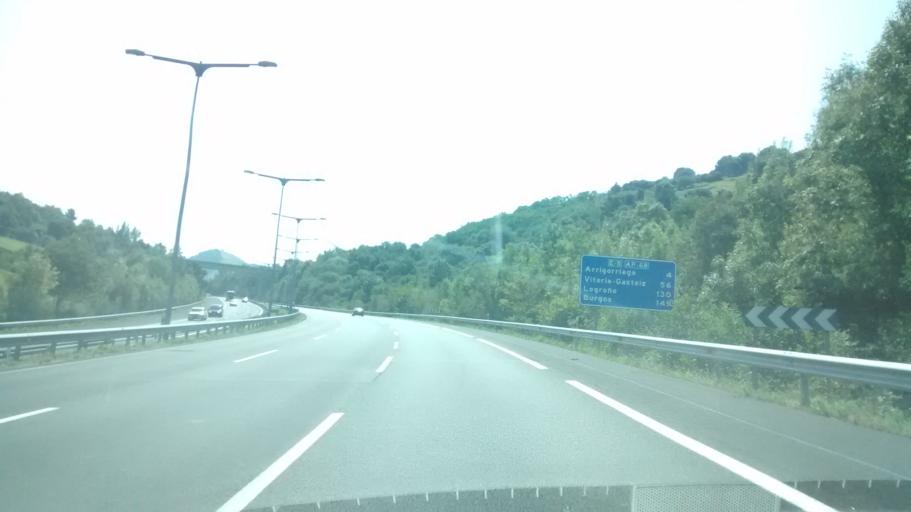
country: ES
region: Basque Country
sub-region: Bizkaia
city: Santutxu
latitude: 43.2243
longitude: -2.9153
